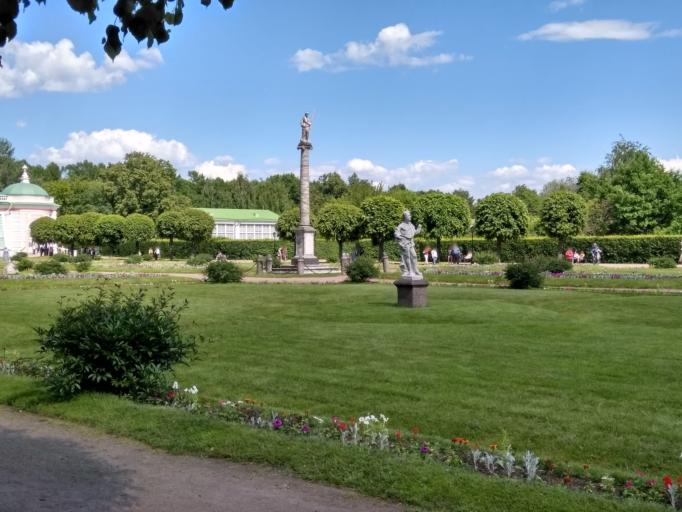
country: RU
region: Moscow
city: Veshnyaki
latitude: 55.7370
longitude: 37.8087
